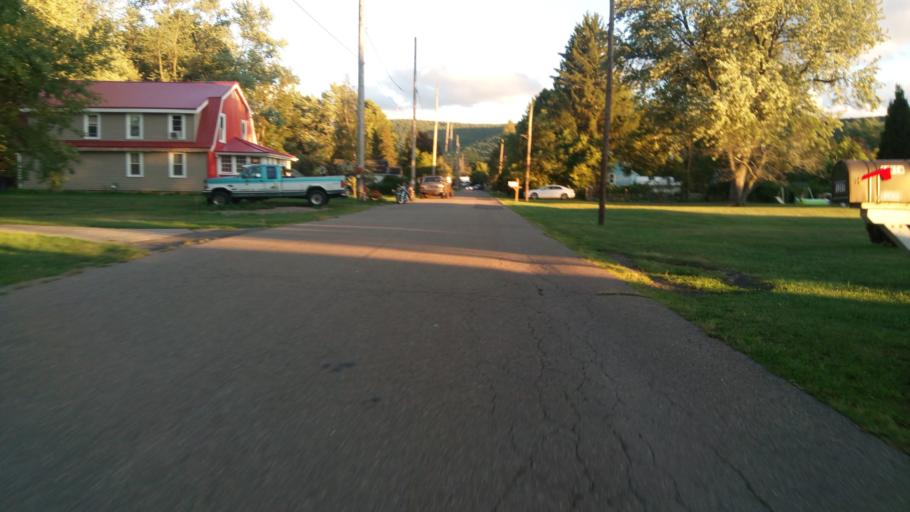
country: US
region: New York
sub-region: Chemung County
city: Southport
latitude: 42.0616
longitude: -76.7920
